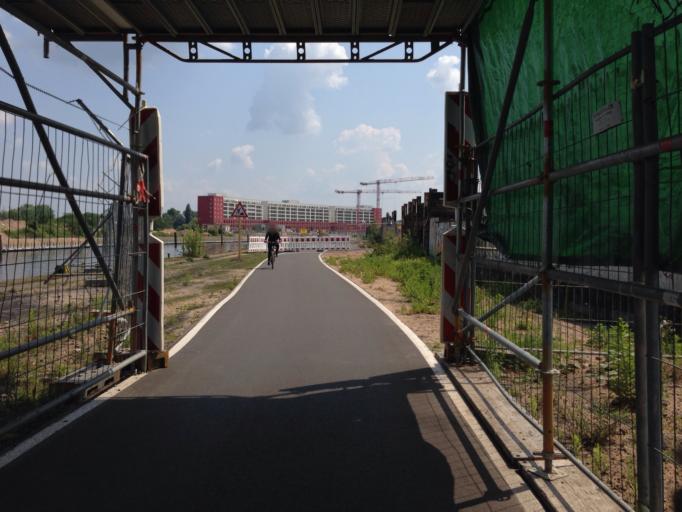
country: DE
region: Hesse
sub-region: Regierungsbezirk Darmstadt
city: Offenbach
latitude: 50.1131
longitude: 8.7451
